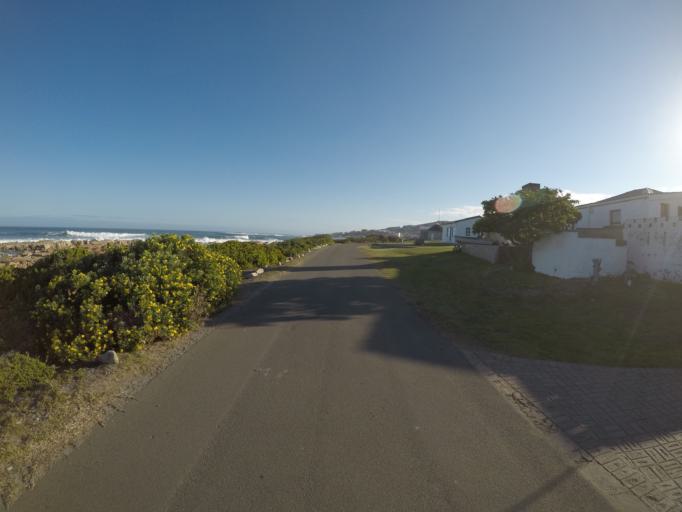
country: ZA
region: Western Cape
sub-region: Eden District Municipality
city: Riversdale
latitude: -34.4260
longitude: 21.3438
